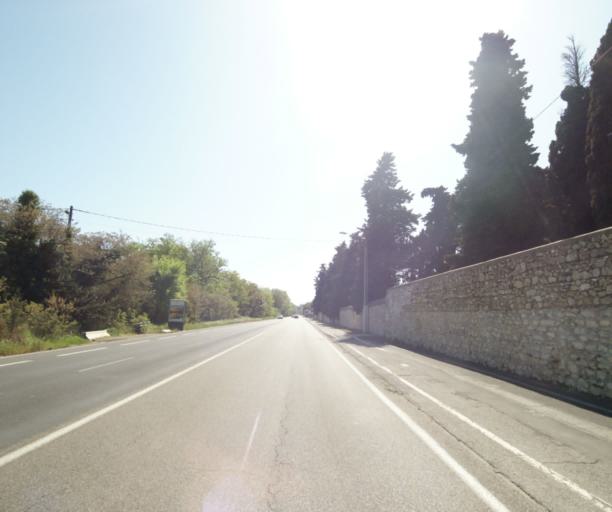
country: FR
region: Languedoc-Roussillon
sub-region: Departement de l'Herault
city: Castelnau-le-Lez
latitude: 43.6250
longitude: 3.8938
